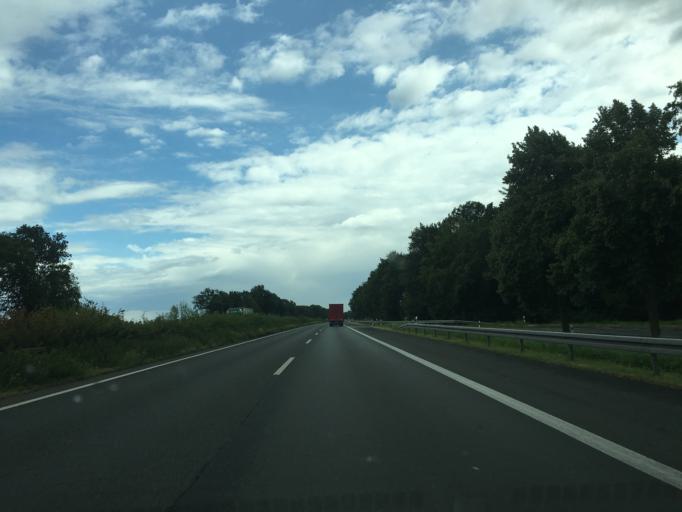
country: DE
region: North Rhine-Westphalia
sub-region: Regierungsbezirk Munster
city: Ascheberg
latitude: 51.8121
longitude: 7.6213
